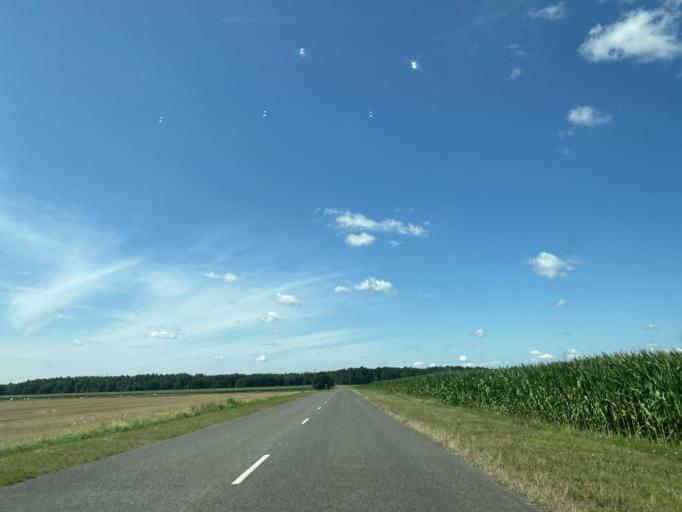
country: BY
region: Brest
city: Ivanava
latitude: 52.2294
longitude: 25.6444
